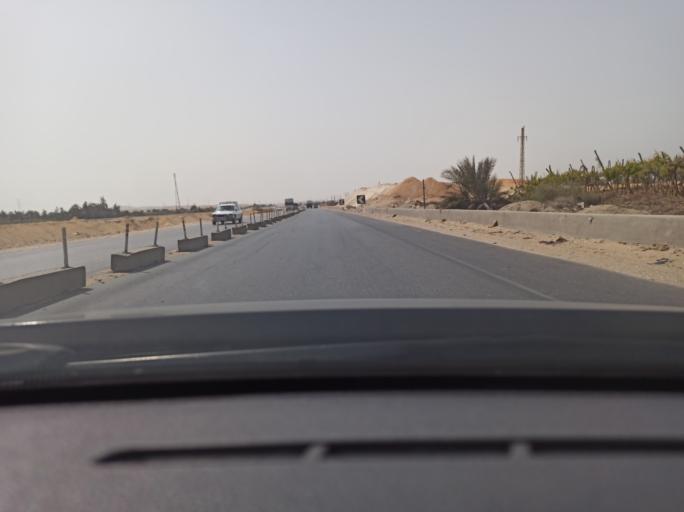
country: EG
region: Muhafazat al Fayyum
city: Al Wasitah
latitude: 29.2712
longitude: 31.2648
